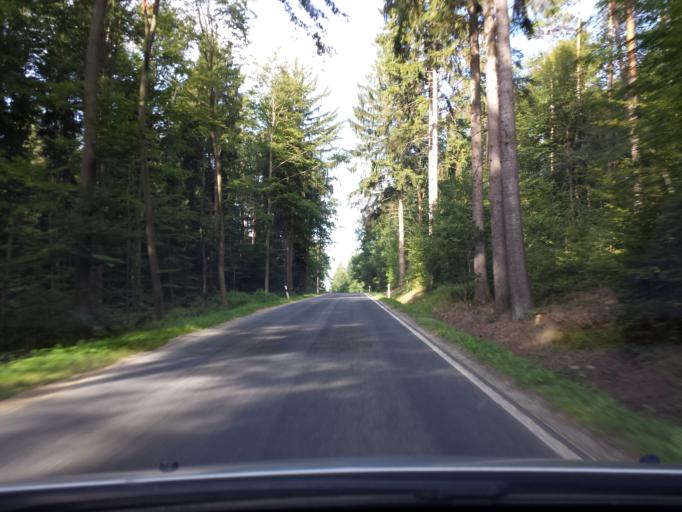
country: DE
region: Hesse
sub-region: Regierungsbezirk Kassel
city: Kirchheim
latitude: 50.8662
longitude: 9.6227
